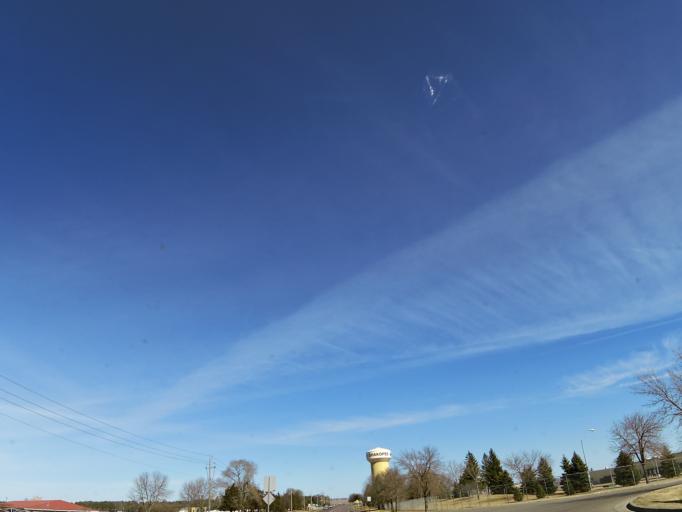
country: US
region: Minnesota
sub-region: Scott County
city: Shakopee
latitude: 44.7869
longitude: -93.4697
